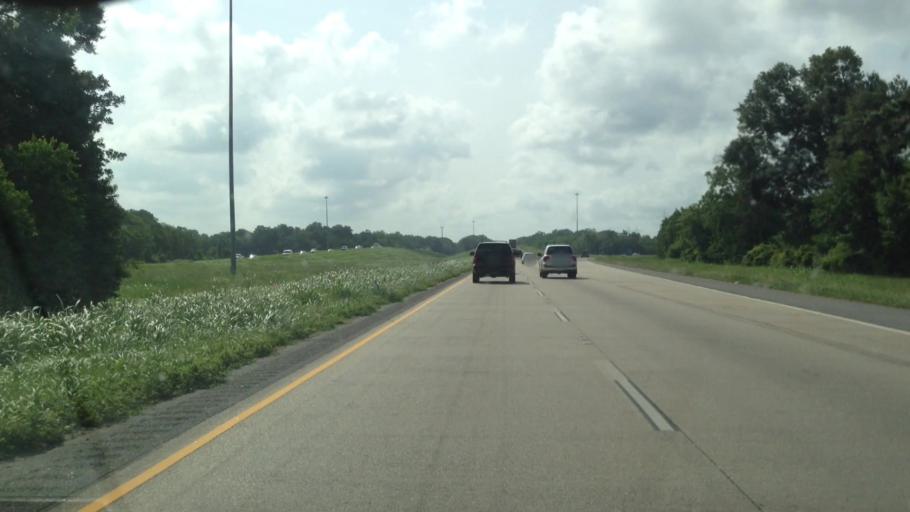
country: US
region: Louisiana
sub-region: Ascension Parish
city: Gonzales
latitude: 30.1949
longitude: -90.9260
